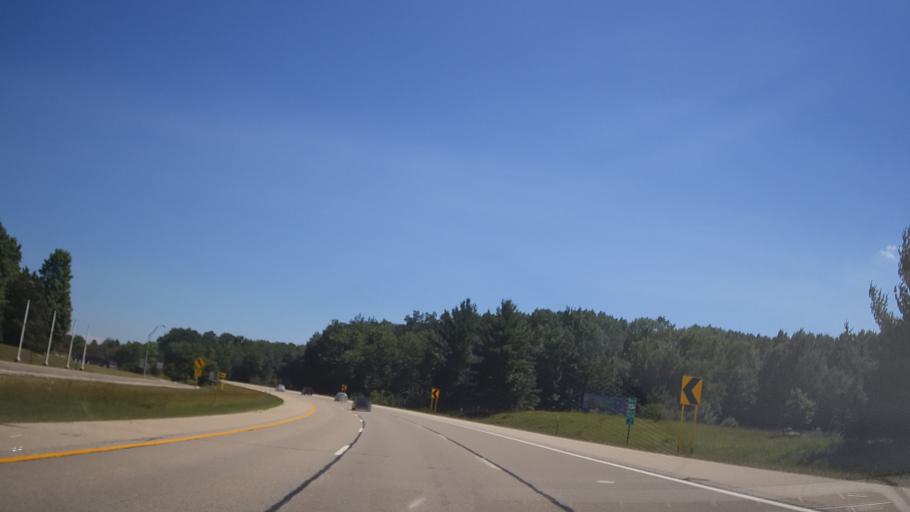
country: US
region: Michigan
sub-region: Clare County
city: Clare
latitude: 43.8525
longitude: -84.7789
